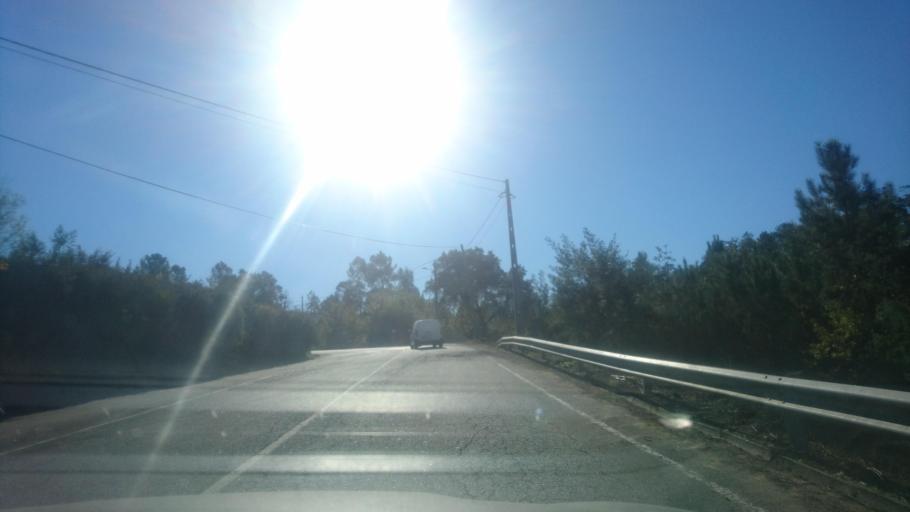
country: PT
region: Aveiro
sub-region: Oliveira de Azemeis
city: Vila Cha
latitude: 40.8684
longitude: -8.4407
